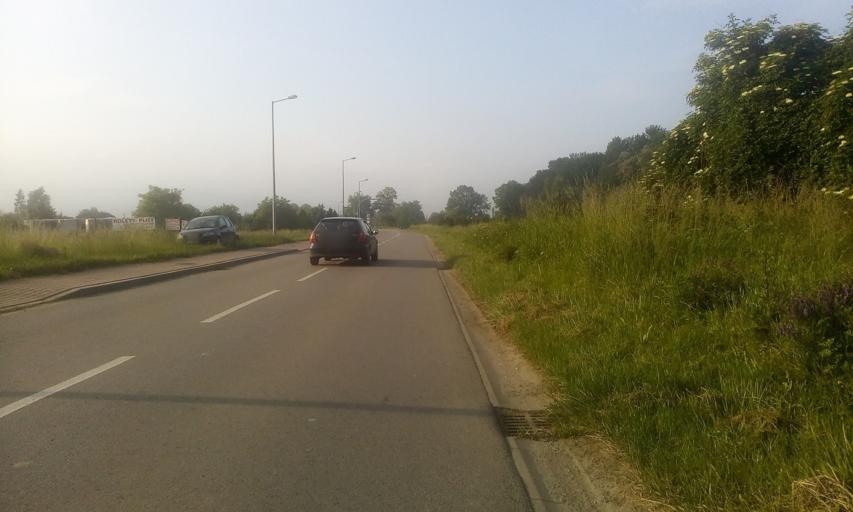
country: PL
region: Lesser Poland Voivodeship
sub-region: Powiat nowosadecki
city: Stary Sacz
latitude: 49.5679
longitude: 20.6384
